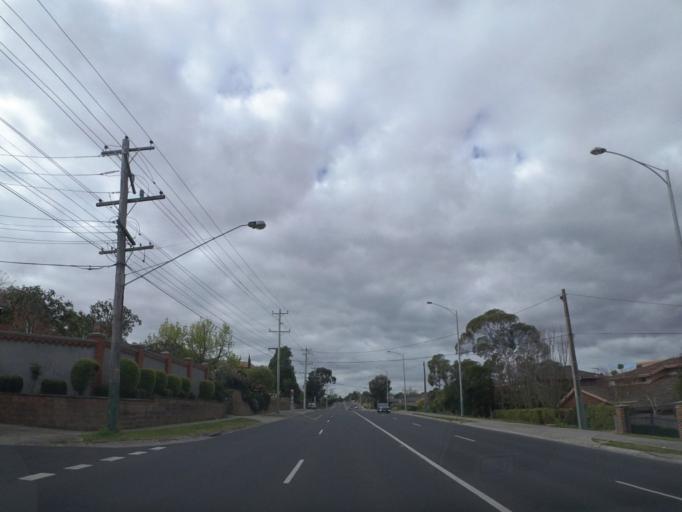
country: AU
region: Victoria
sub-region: Boroondara
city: Balwyn North
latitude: -37.7844
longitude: 145.1076
